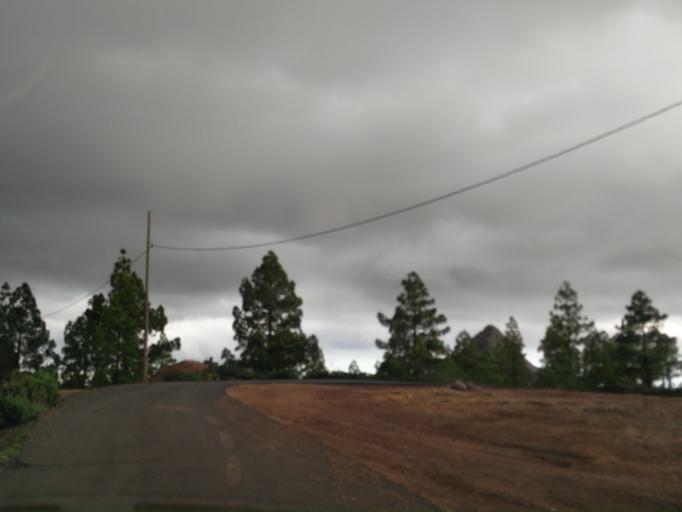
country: ES
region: Canary Islands
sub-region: Provincia de Santa Cruz de Tenerife
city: Arona
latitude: 28.1291
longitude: -16.6918
